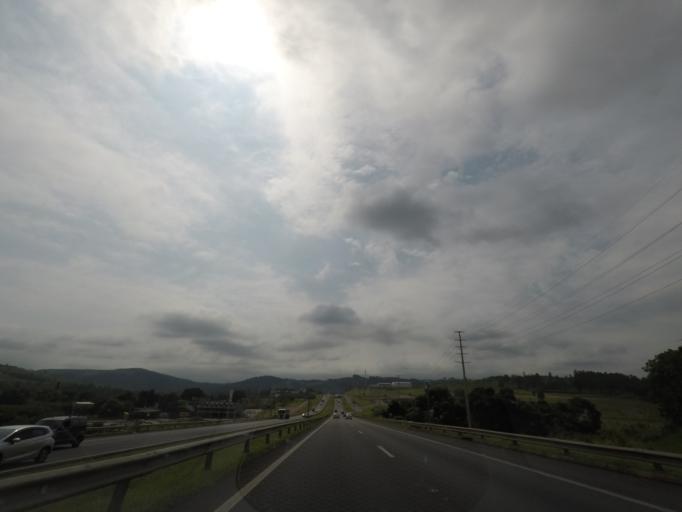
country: BR
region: Sao Paulo
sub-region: Valinhos
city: Valinhos
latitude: -22.9070
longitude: -46.9748
